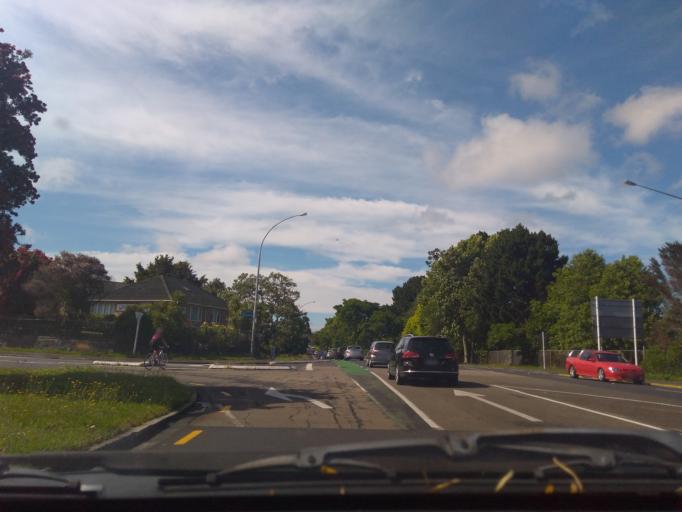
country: NZ
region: Auckland
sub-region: Auckland
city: Auckland
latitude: -36.8703
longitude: 174.7258
